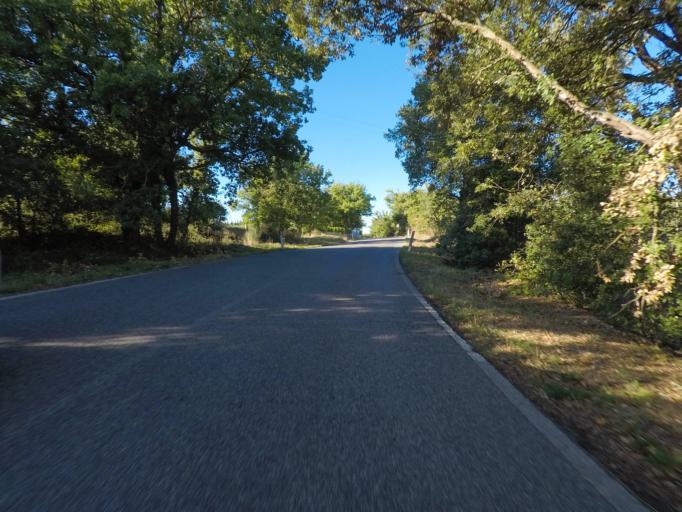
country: IT
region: Tuscany
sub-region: Provincia di Siena
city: Belverde
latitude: 43.4041
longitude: 11.3526
